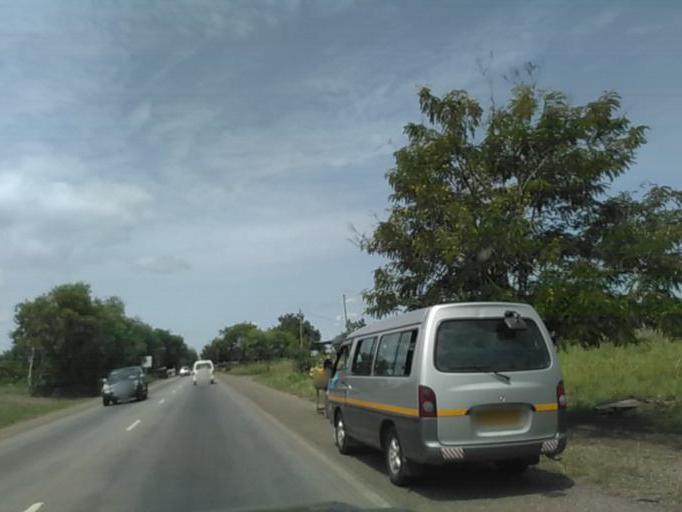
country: GH
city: Akropong
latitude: 6.1005
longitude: 0.0458
